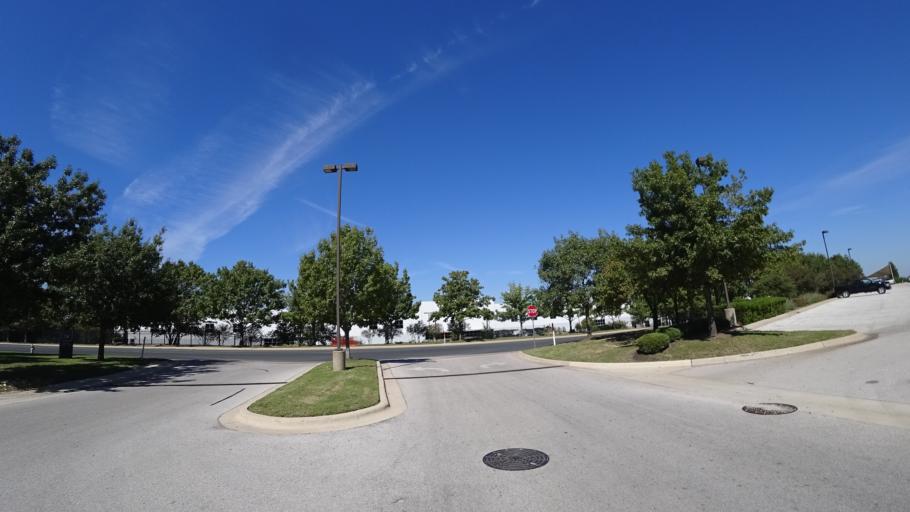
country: US
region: Texas
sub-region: Travis County
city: Austin
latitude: 30.2112
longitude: -97.6954
